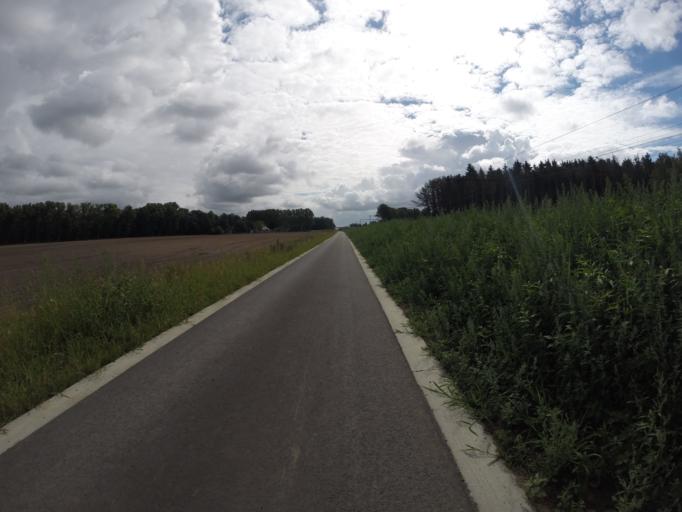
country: BE
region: Flanders
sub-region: Provincie Oost-Vlaanderen
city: Knesselare
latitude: 51.1015
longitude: 3.4061
